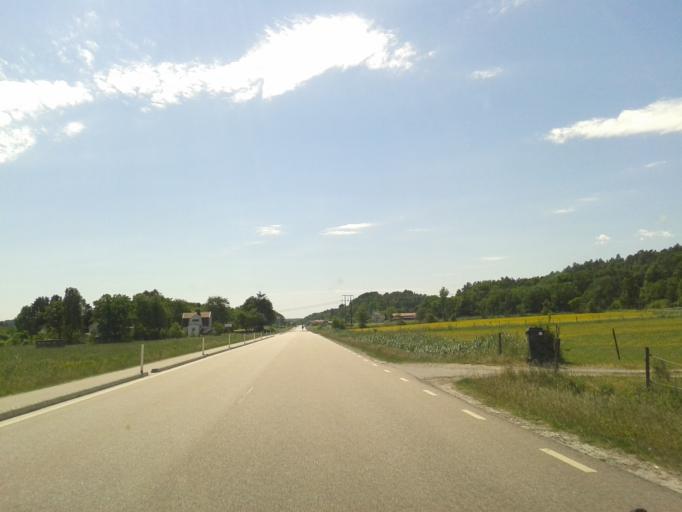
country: SE
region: Vaestra Goetaland
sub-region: Stenungsunds Kommun
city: Stora Hoga
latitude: 58.0365
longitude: 11.8827
